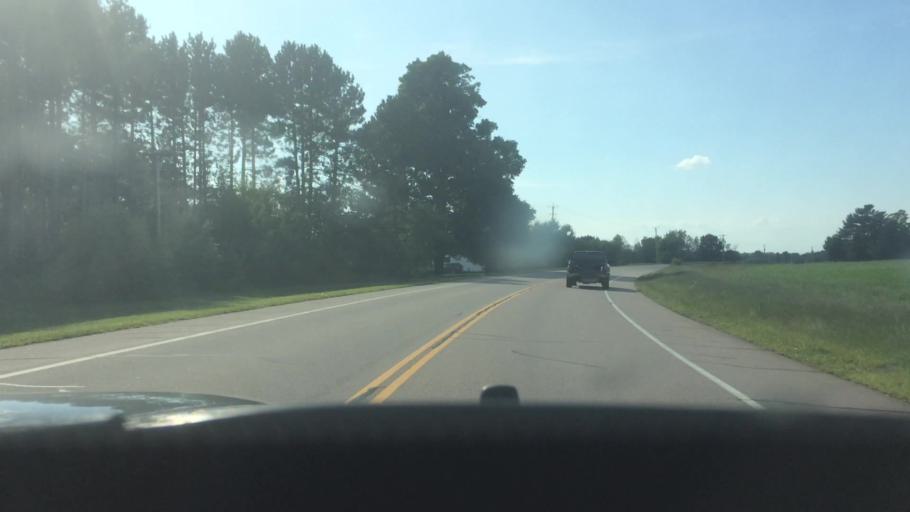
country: US
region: New York
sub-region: Franklin County
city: Malone
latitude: 44.8445
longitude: -74.1912
